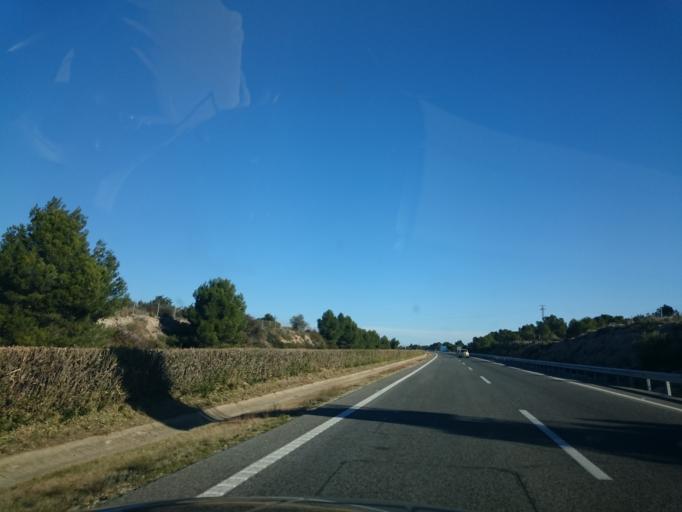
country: ES
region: Catalonia
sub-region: Provincia de Tarragona
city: l'Ametlla de Mar
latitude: 40.8744
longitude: 0.7868
